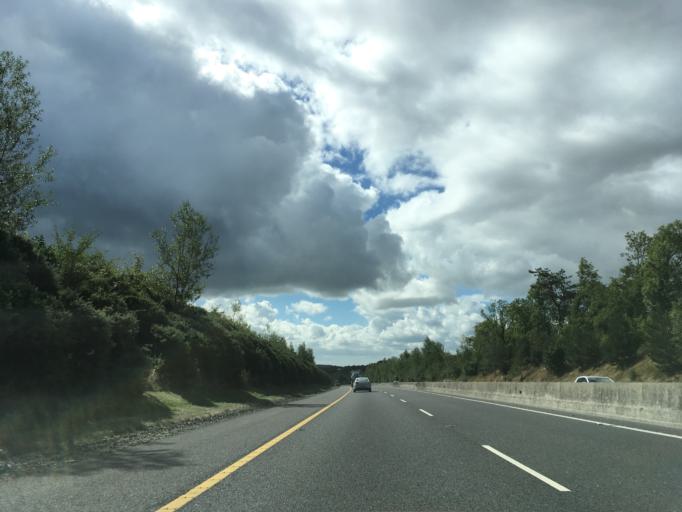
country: IE
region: Munster
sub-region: County Cork
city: Fermoy
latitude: 52.1772
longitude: -8.2716
